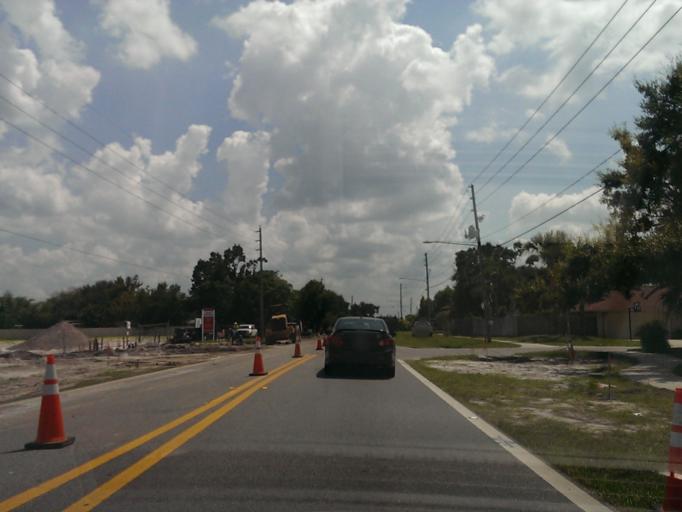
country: US
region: Florida
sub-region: Orange County
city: Doctor Phillips
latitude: 28.4901
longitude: -81.4752
